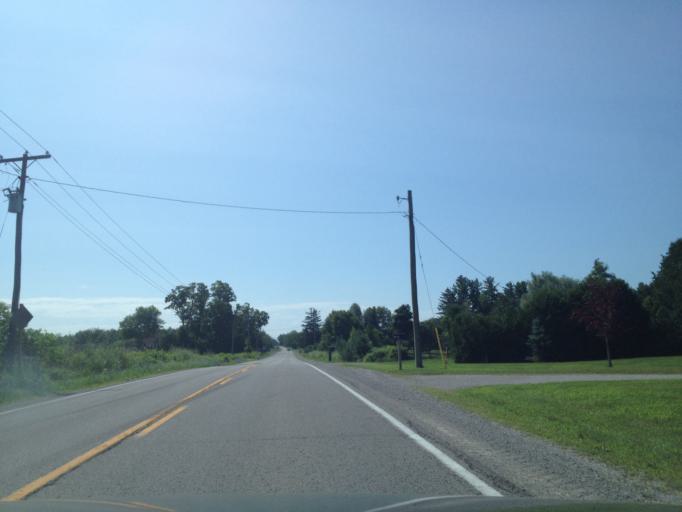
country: CA
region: Ontario
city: Norfolk County
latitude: 42.7854
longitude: -80.4053
